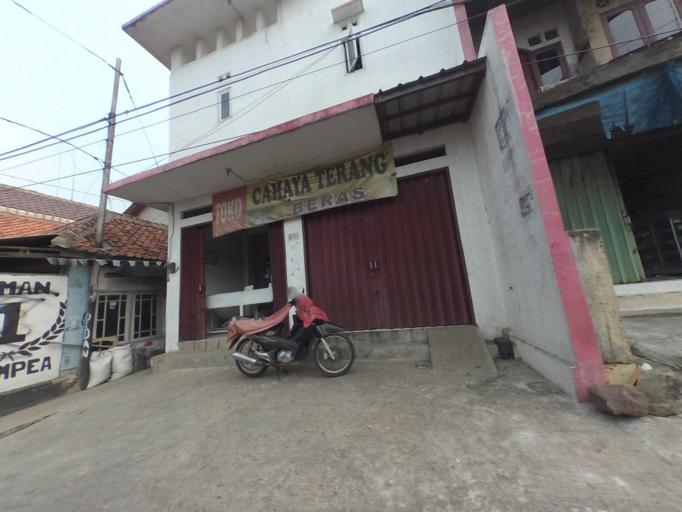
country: ID
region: West Java
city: Ciampea
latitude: -6.5745
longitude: 106.6640
